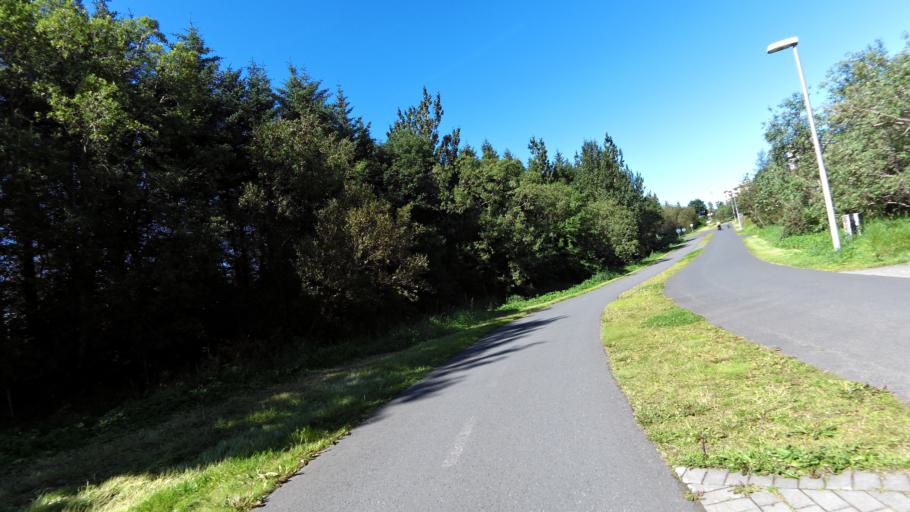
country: IS
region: Capital Region
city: Reykjavik
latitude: 64.1183
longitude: -21.8884
